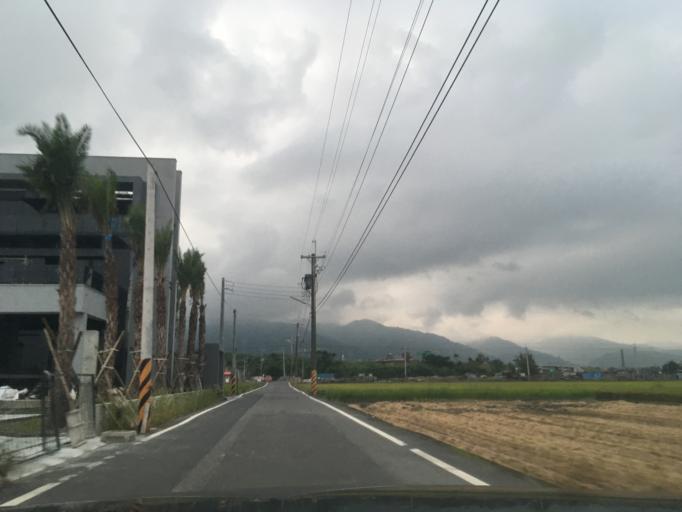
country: TW
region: Taiwan
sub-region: Yilan
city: Yilan
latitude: 24.8200
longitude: 121.7865
